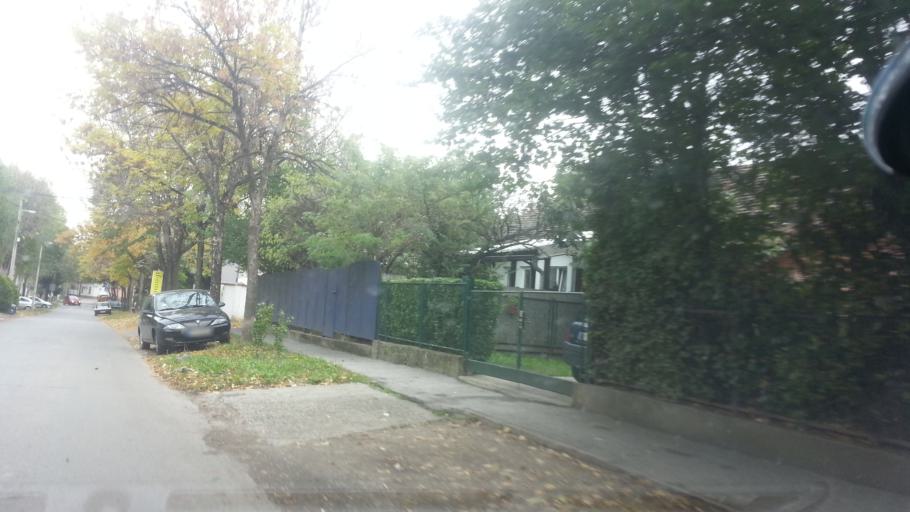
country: RS
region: Central Serbia
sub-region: Belgrade
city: Zemun
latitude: 44.8385
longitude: 20.3966
